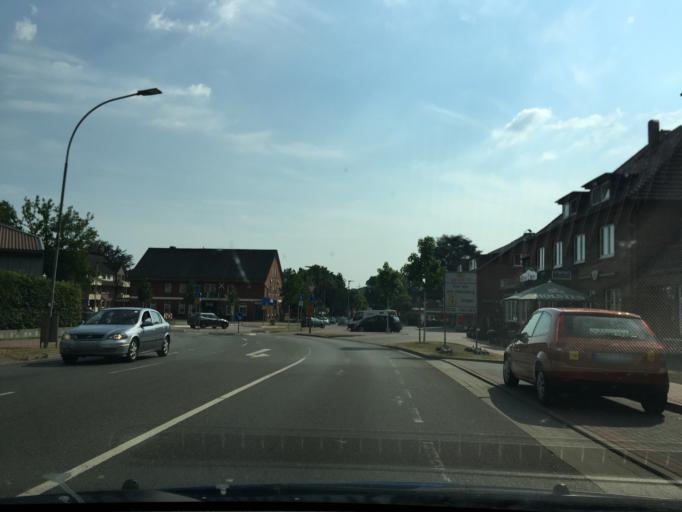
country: DE
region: Lower Saxony
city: Buchholz in der Nordheide
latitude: 53.3800
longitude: 9.8963
